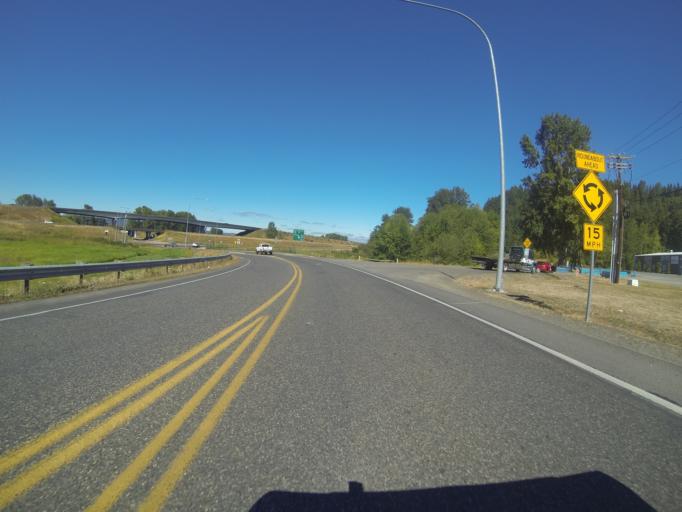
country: US
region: Washington
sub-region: Cowlitz County
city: Woodland
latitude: 45.9280
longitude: -122.7536
